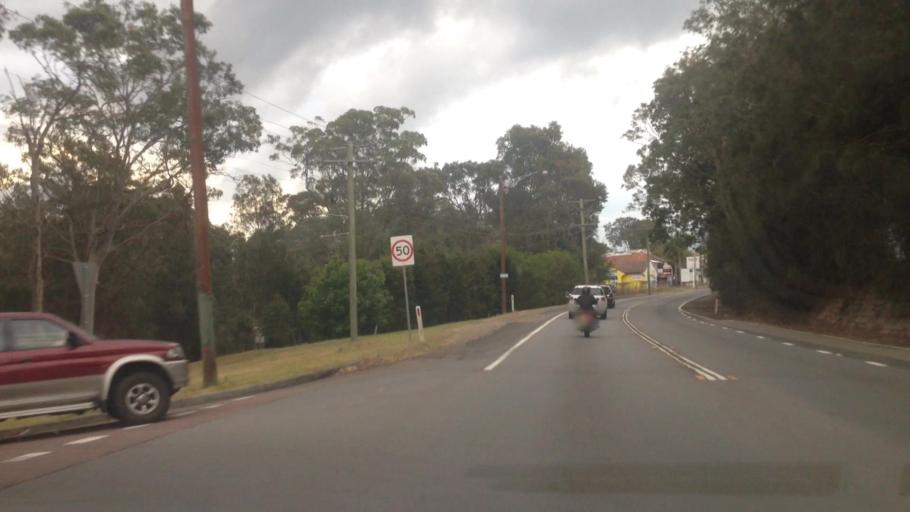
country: AU
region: New South Wales
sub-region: Wyong Shire
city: Chittaway Bay
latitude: -33.2892
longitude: 151.4241
